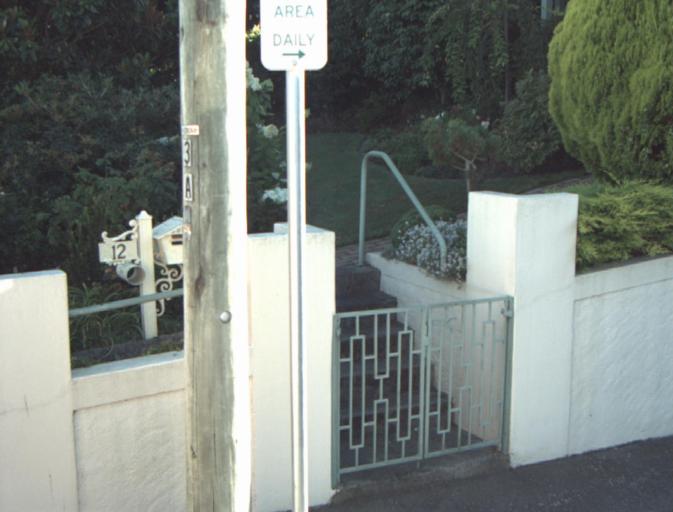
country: AU
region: Tasmania
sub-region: Launceston
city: East Launceston
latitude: -41.4371
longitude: 147.1450
